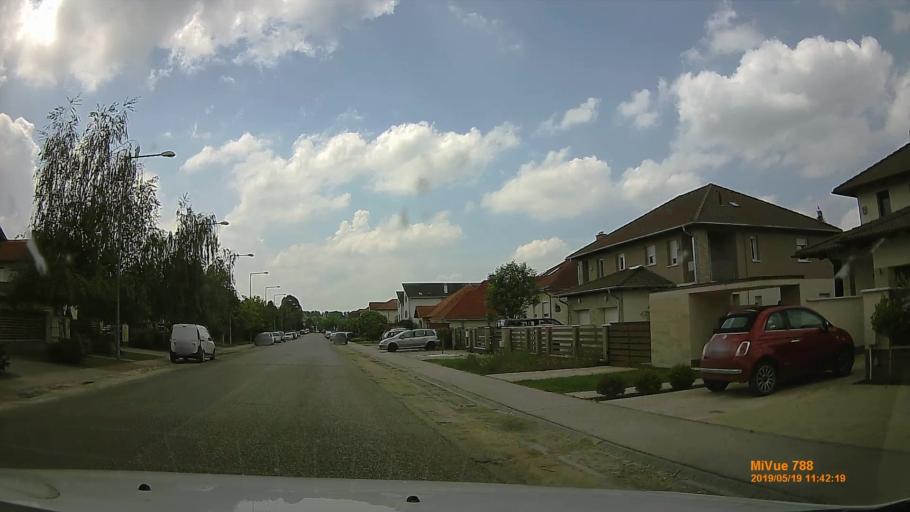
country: HU
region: Budapest
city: Budapest XVII. keruelet
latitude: 47.4715
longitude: 19.2288
